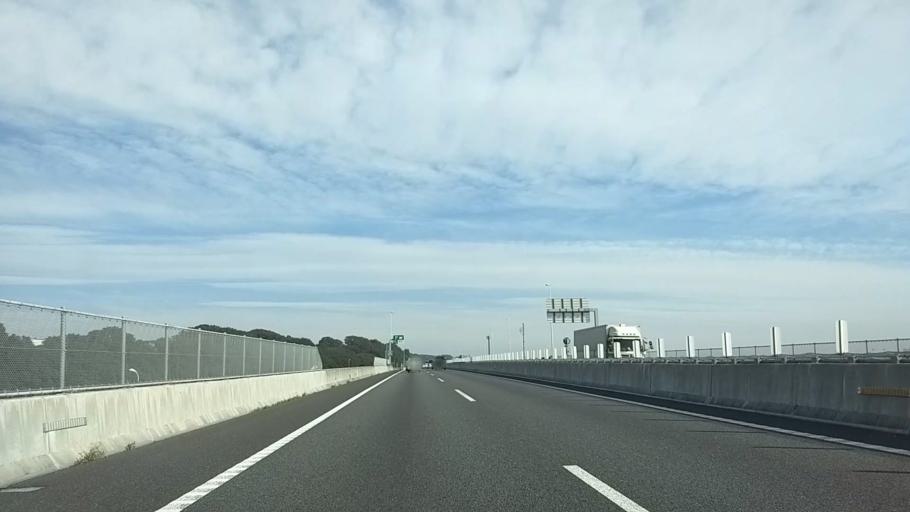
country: JP
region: Kanagawa
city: Zama
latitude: 35.4853
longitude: 139.3709
